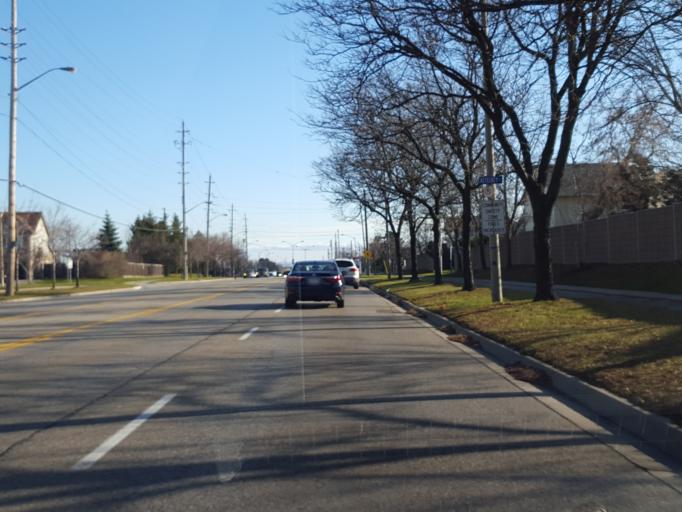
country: CA
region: Ontario
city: Burlington
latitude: 43.3736
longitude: -79.7982
